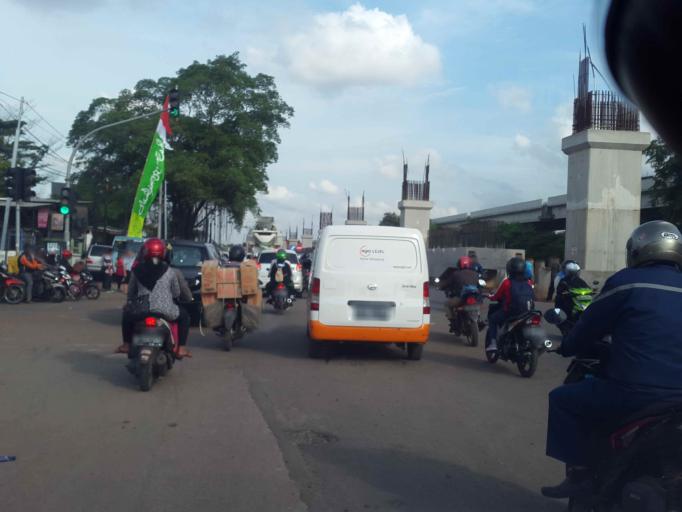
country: ID
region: West Java
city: Bekasi
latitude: -6.2489
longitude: 106.9354
